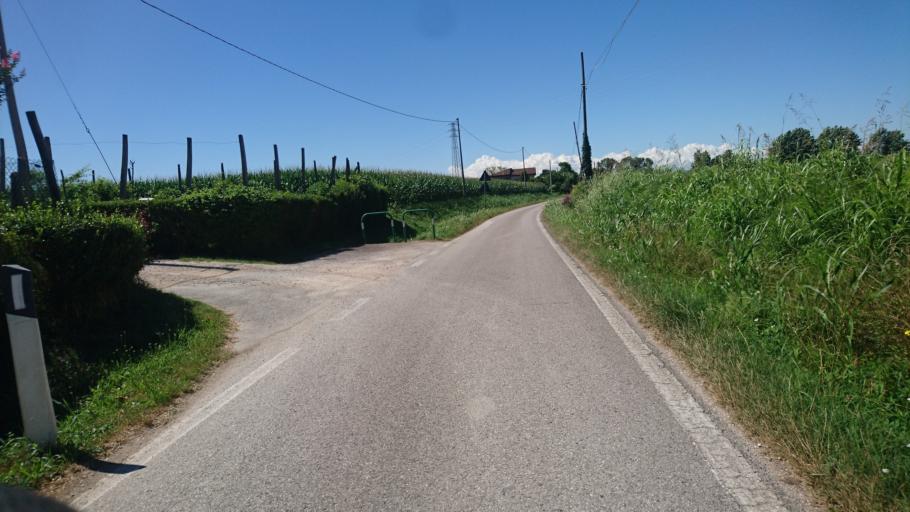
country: IT
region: Veneto
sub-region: Provincia di Padova
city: Campagnola
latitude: 45.2728
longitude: 12.0190
